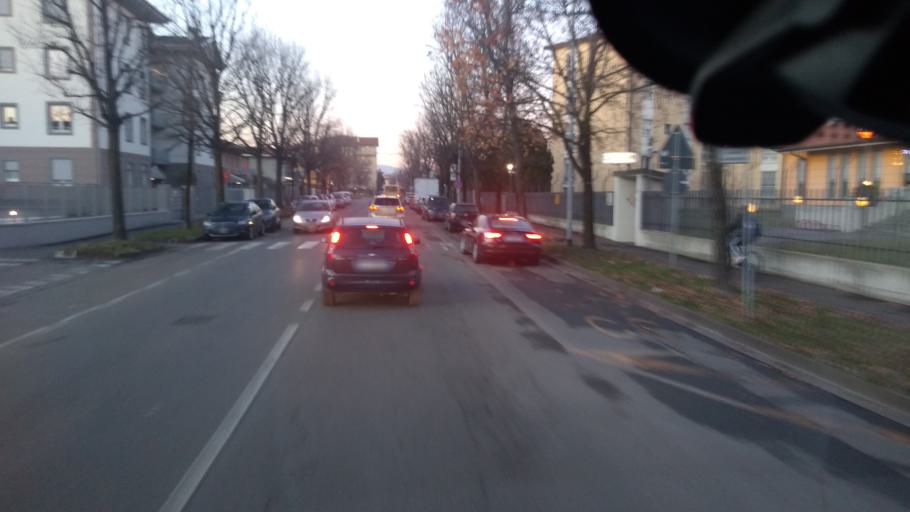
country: IT
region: Lombardy
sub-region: Provincia di Bergamo
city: Treviglio
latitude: 45.5231
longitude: 9.5996
